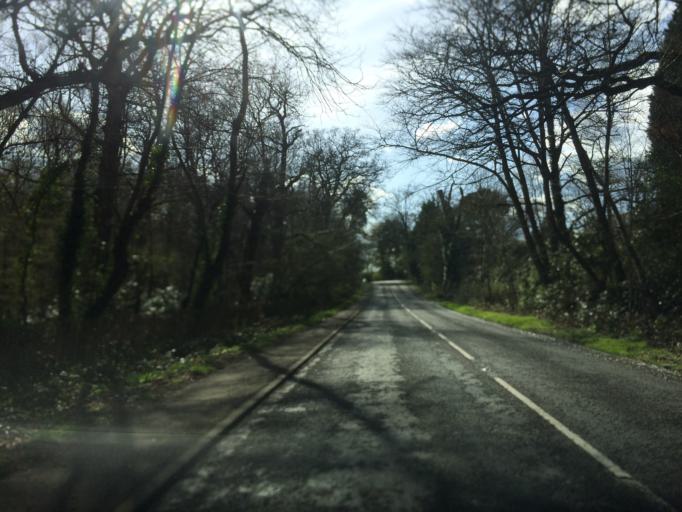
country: GB
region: England
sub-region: Surrey
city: Ottershaw
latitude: 51.3613
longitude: -0.5454
